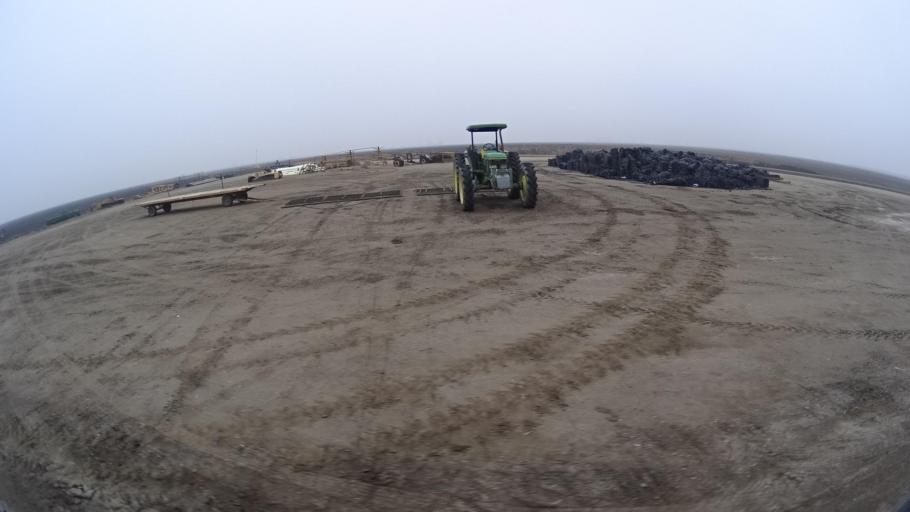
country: US
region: California
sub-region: Kern County
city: Buttonwillow
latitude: 35.4124
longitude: -119.5040
